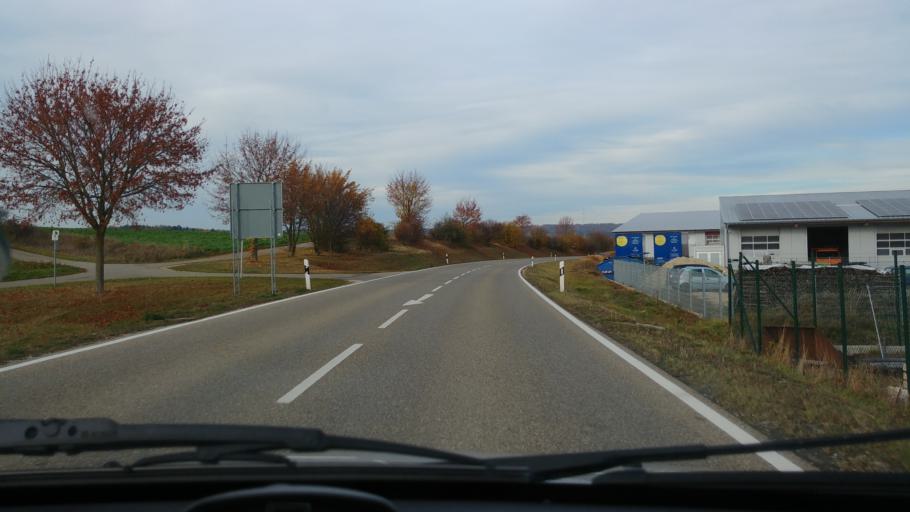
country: DE
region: Bavaria
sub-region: Swabia
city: Bachhagel
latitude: 48.6386
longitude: 10.2954
